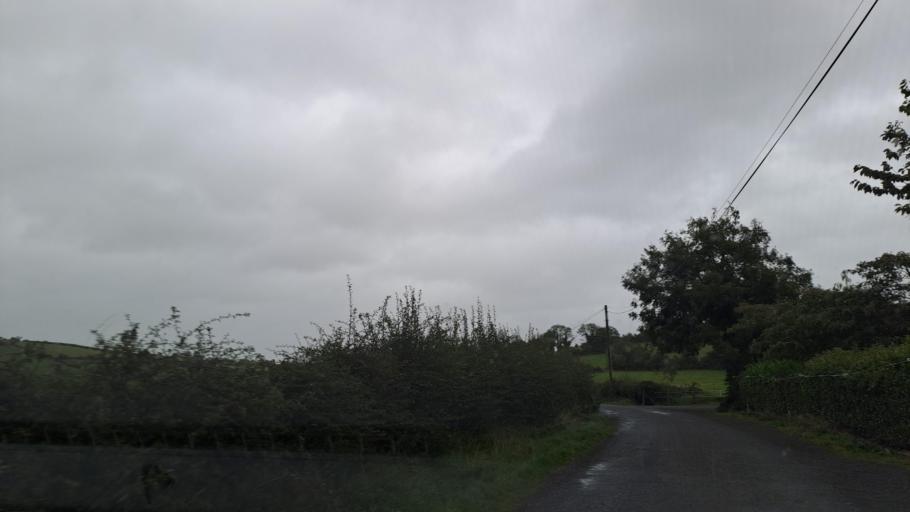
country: IE
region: Ulster
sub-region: An Cabhan
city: Kingscourt
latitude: 54.0077
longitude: -6.8222
